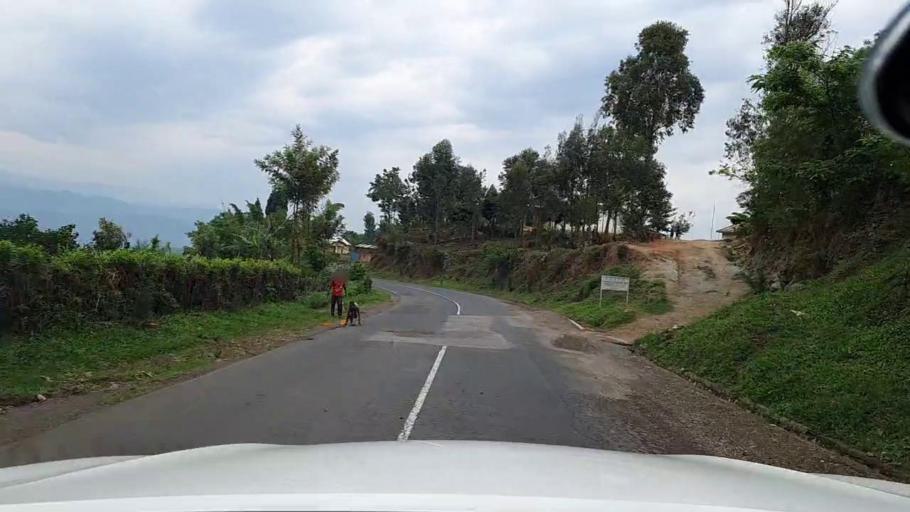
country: RW
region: Western Province
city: Cyangugu
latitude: -2.6597
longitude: 28.9788
